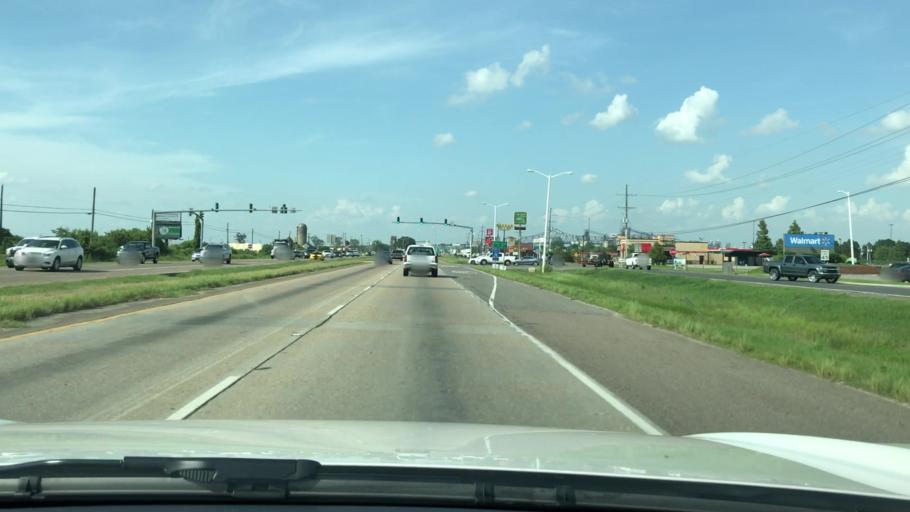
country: US
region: Louisiana
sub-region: West Baton Rouge Parish
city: Port Allen
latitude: 30.4205
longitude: -91.2199
